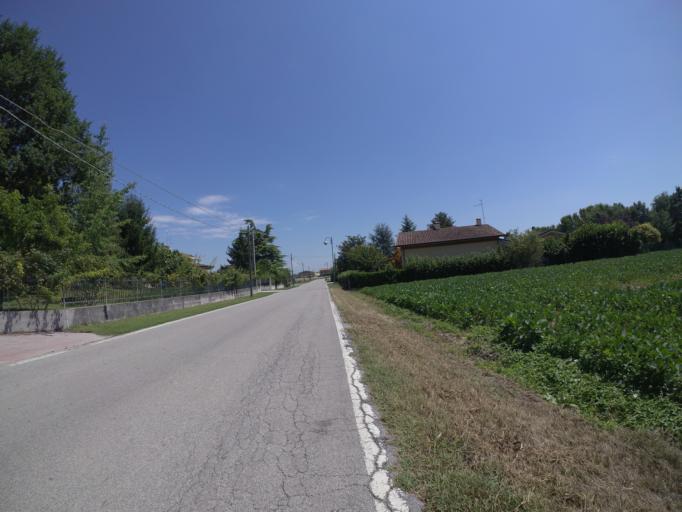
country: IT
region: Friuli Venezia Giulia
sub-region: Provincia di Udine
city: Pocenia
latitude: 45.8697
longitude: 13.0929
